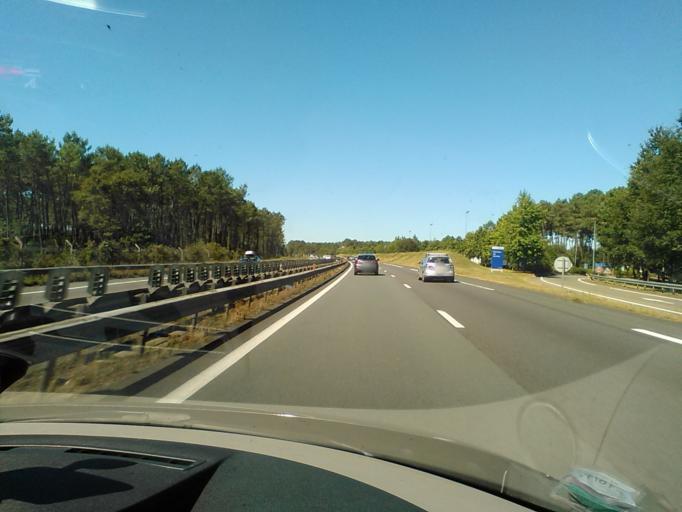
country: FR
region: Aquitaine
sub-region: Departement des Landes
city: Saint-Vincent-de-Tyrosse
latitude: 43.6805
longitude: -1.3018
